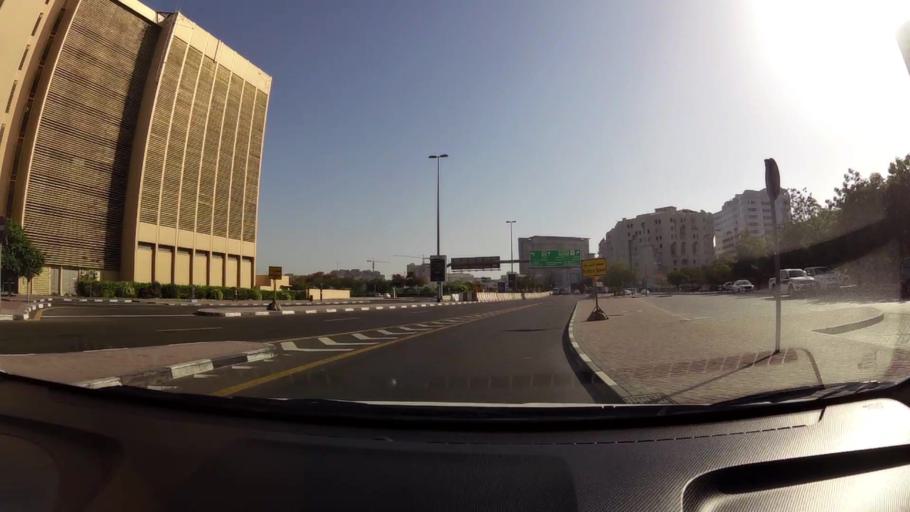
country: AE
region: Ash Shariqah
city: Sharjah
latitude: 25.2631
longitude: 55.3136
